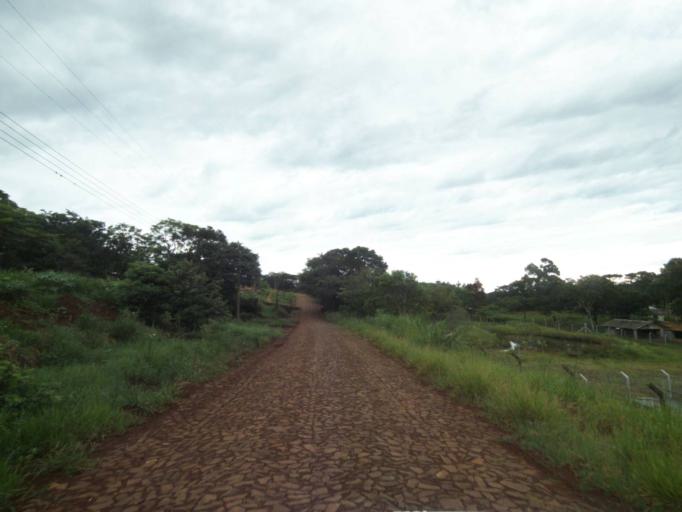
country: BR
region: Parana
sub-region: Guaraniacu
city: Guaraniacu
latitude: -25.1167
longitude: -52.8552
